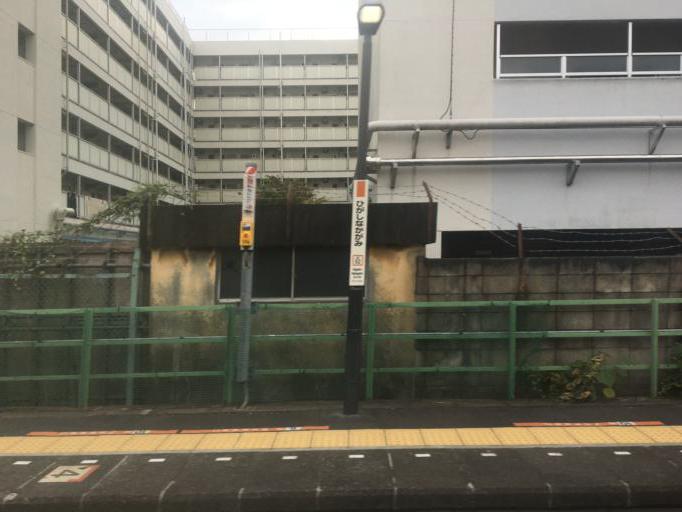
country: JP
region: Tokyo
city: Hino
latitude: 35.7066
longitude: 139.3837
